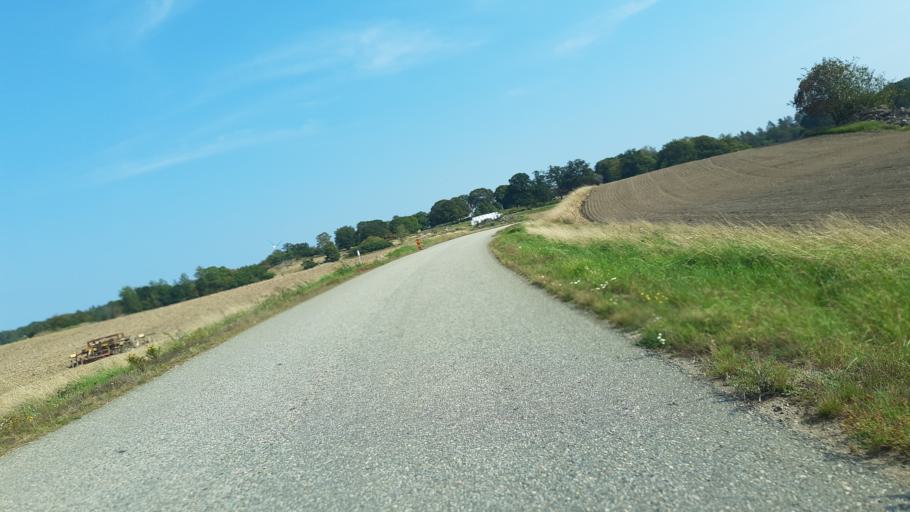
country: SE
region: Blekinge
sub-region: Ronneby Kommun
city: Brakne-Hoby
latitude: 56.1969
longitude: 15.1145
